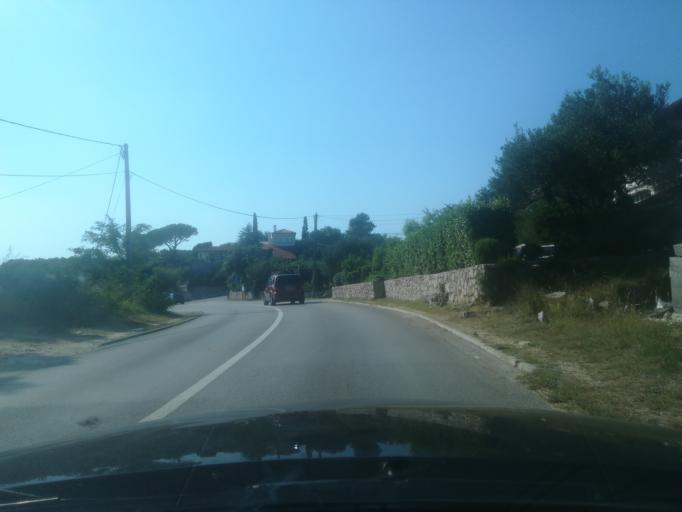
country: HR
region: Primorsko-Goranska
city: Banjol
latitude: 44.7534
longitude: 14.7793
